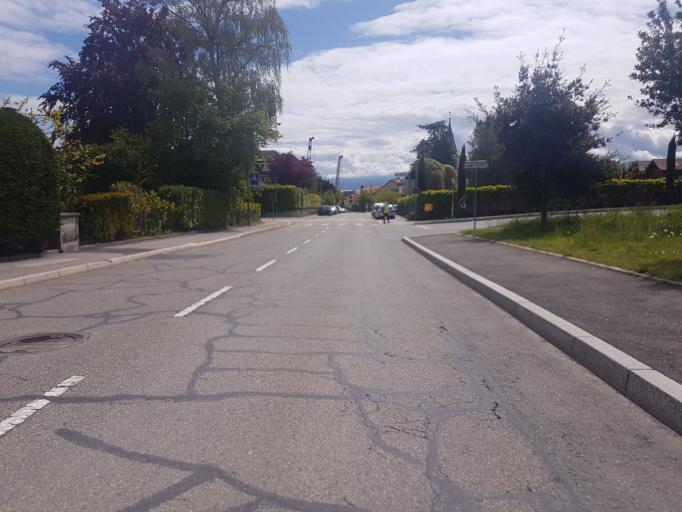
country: CH
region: Vaud
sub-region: Nyon District
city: Rolle
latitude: 46.4592
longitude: 6.3344
